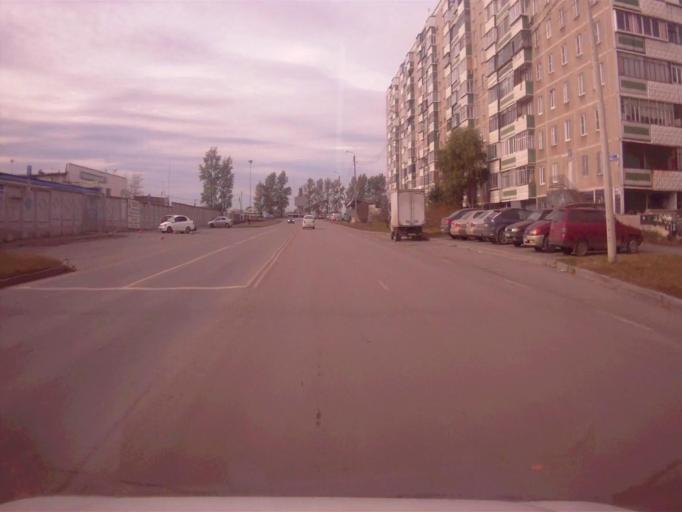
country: RU
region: Chelyabinsk
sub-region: Gorod Chelyabinsk
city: Chelyabinsk
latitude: 55.1175
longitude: 61.4225
